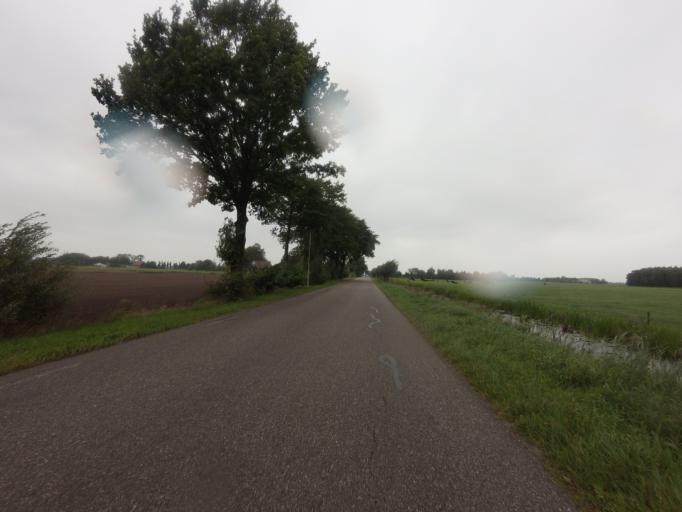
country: NL
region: Friesland
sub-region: Gemeente Opsterland
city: Tijnje
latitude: 53.0267
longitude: 5.9831
